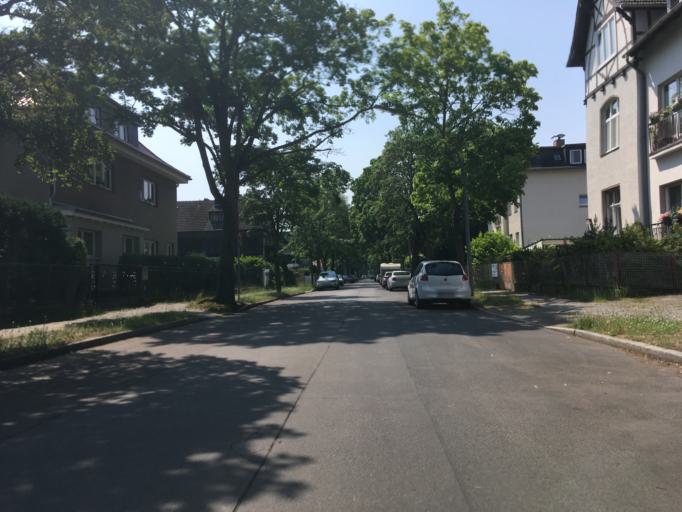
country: DE
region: Berlin
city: Konradshohe
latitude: 52.5728
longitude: 13.2291
